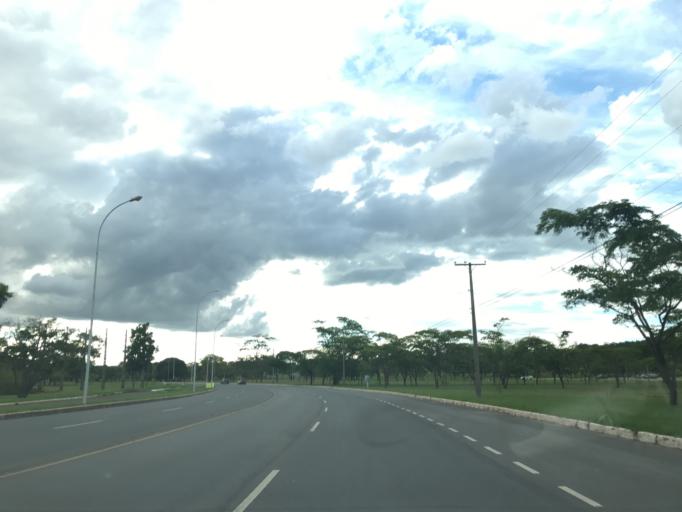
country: BR
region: Federal District
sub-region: Brasilia
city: Brasilia
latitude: -15.8114
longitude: -47.9178
